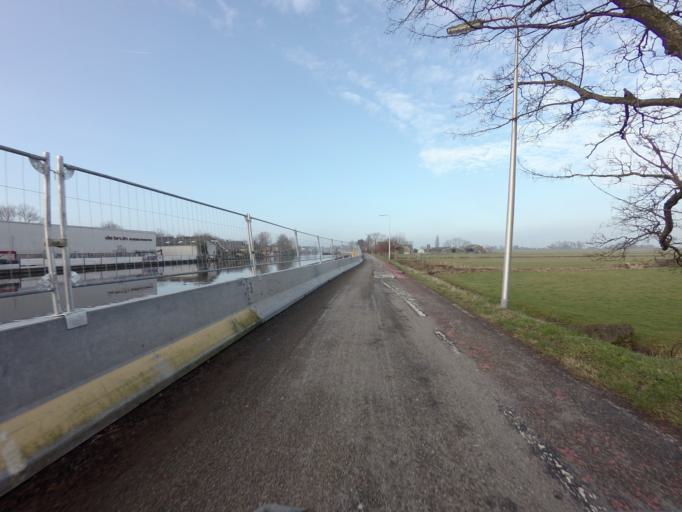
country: NL
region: South Holland
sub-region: Bodegraven-Reeuwijk
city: Bodegraven
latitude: 52.0997
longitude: 4.7374
